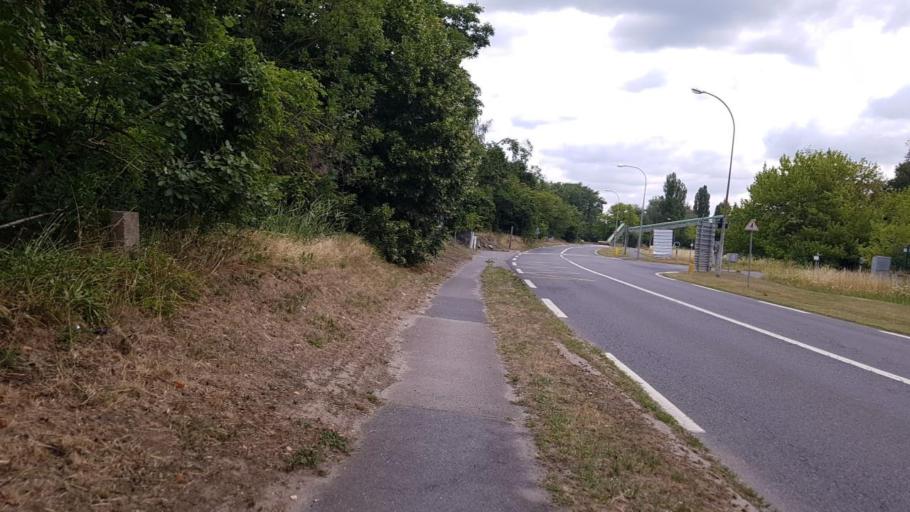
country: FR
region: Picardie
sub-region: Departement de l'Oise
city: Clairoix
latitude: 49.4334
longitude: 2.8446
